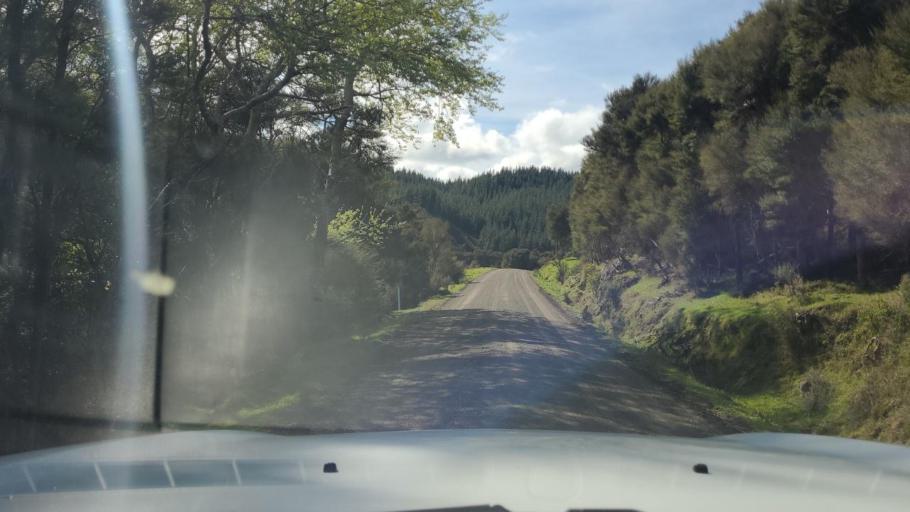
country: NZ
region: Wellington
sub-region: South Wairarapa District
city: Waipawa
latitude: -41.3487
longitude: 175.6978
